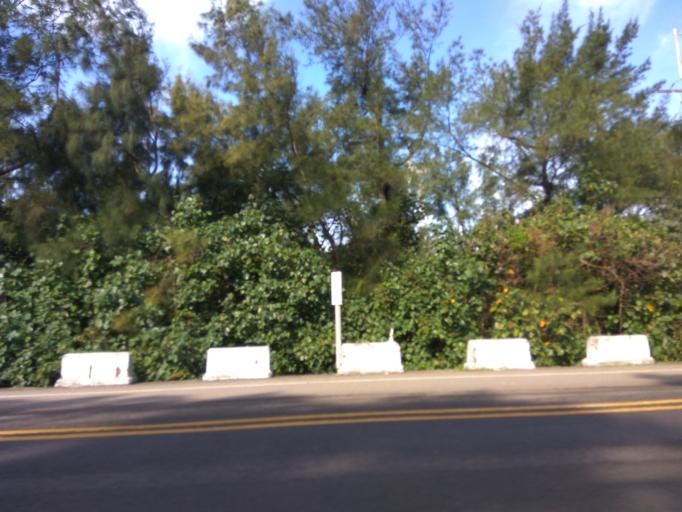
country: TW
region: Taiwan
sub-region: Hsinchu
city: Zhubei
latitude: 25.0301
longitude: 121.0476
